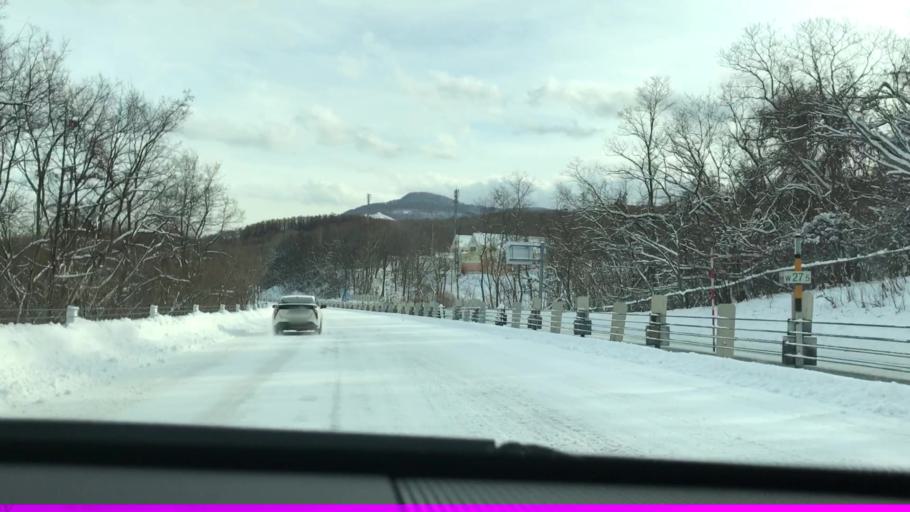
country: JP
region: Hokkaido
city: Otaru
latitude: 43.1482
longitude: 141.1311
